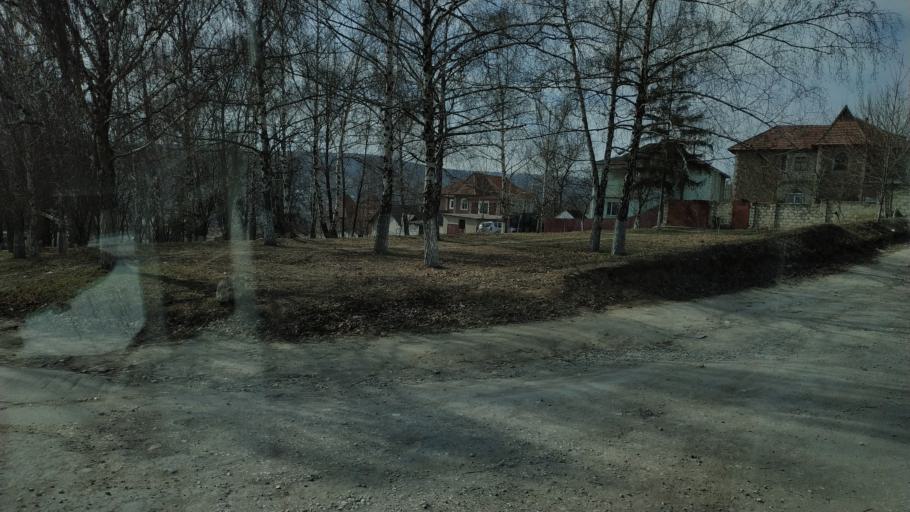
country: MD
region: Chisinau
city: Vatra
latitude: 47.0958
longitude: 28.6740
